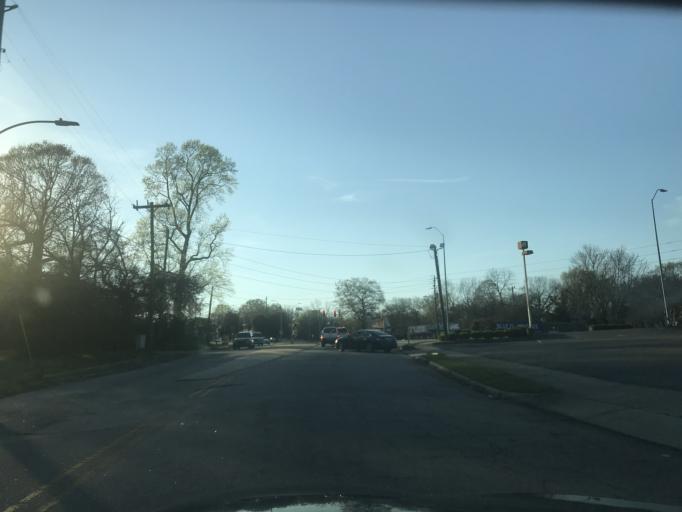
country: US
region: North Carolina
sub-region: Wake County
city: Raleigh
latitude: 35.7793
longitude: -78.6183
